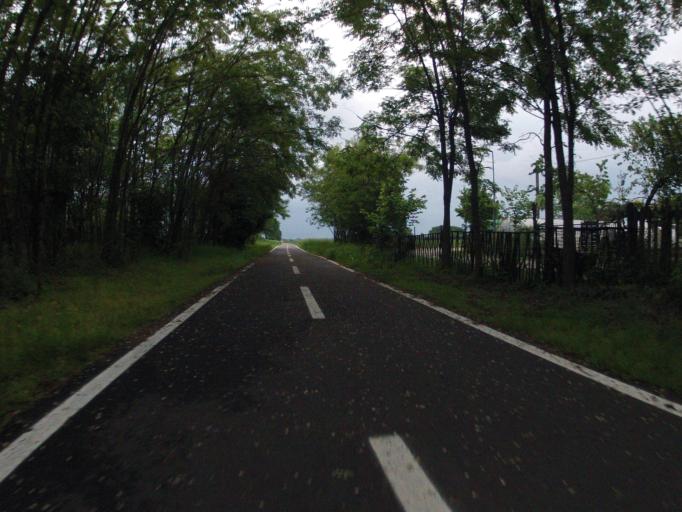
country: IT
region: Piedmont
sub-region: Provincia di Torino
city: Villafranca Piemonte
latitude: 44.7876
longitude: 7.5096
